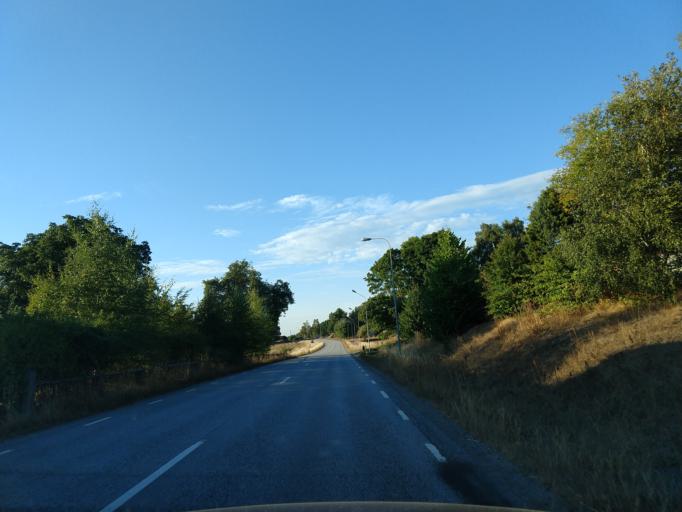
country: SE
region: Blekinge
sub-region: Ronneby Kommun
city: Brakne-Hoby
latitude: 56.2402
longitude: 15.1174
